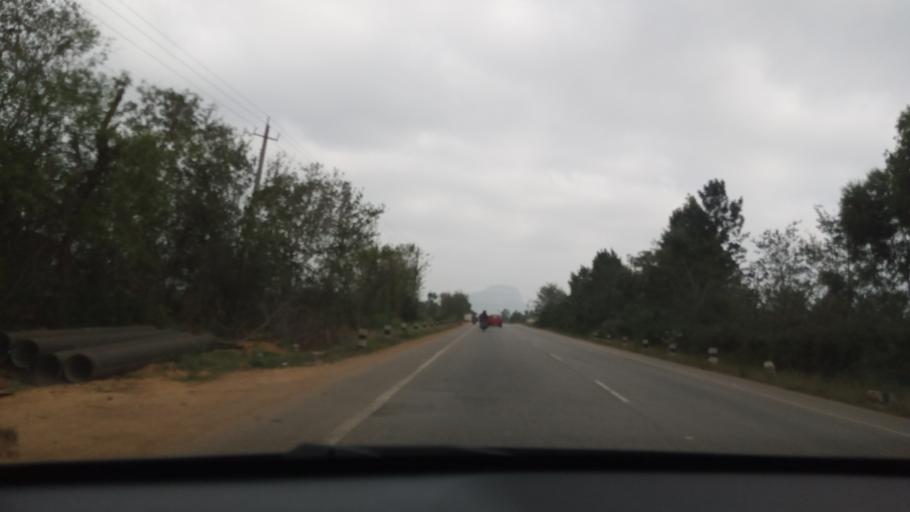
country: IN
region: Karnataka
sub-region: Chikkaballapur
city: Chintamani
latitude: 13.3013
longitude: 77.9710
